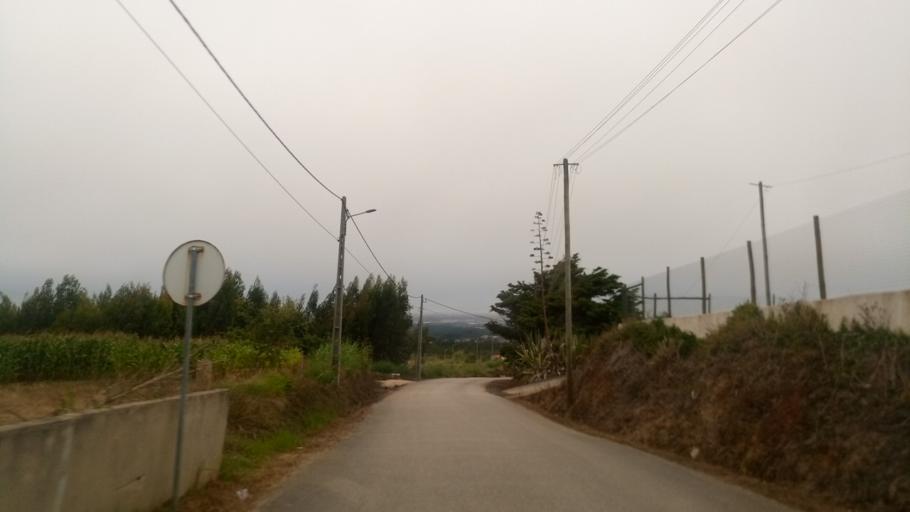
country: PT
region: Leiria
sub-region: Caldas da Rainha
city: Caldas da Rainha
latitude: 39.4608
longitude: -9.1915
